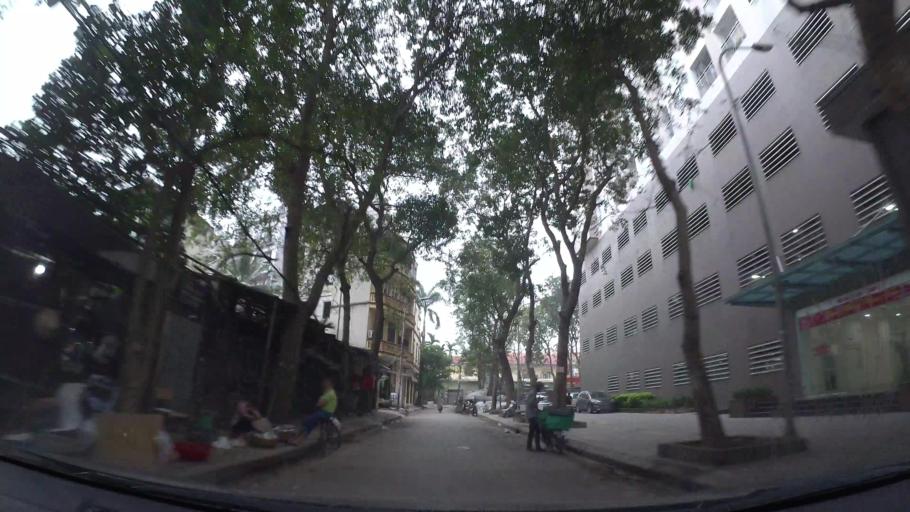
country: VN
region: Ha Noi
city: Hai BaTrung
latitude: 20.9898
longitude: 105.8327
